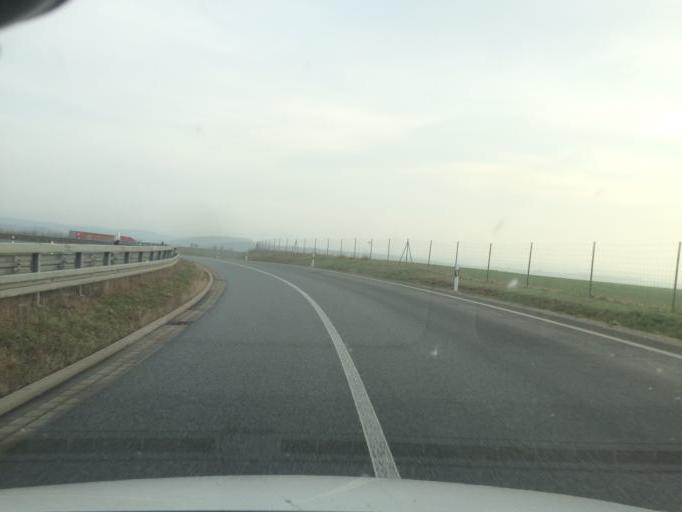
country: DE
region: Thuringia
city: Nohra
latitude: 51.4882
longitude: 10.7208
